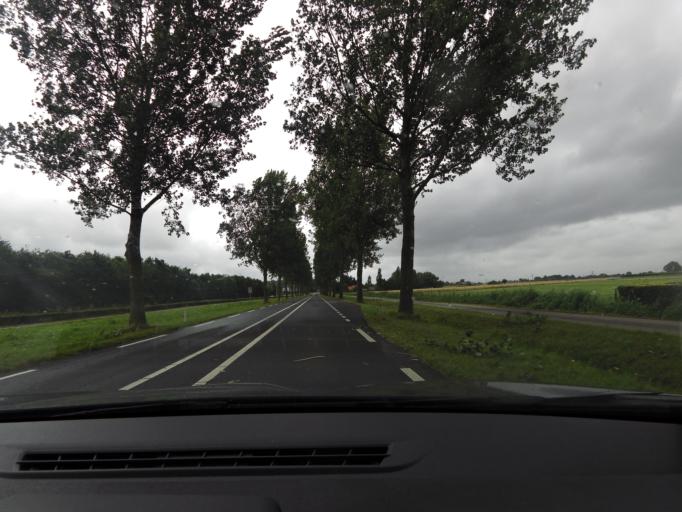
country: NL
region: South Holland
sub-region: Gemeente Hellevoetsluis
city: Nieuwenhoorn
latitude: 51.8569
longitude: 4.1602
